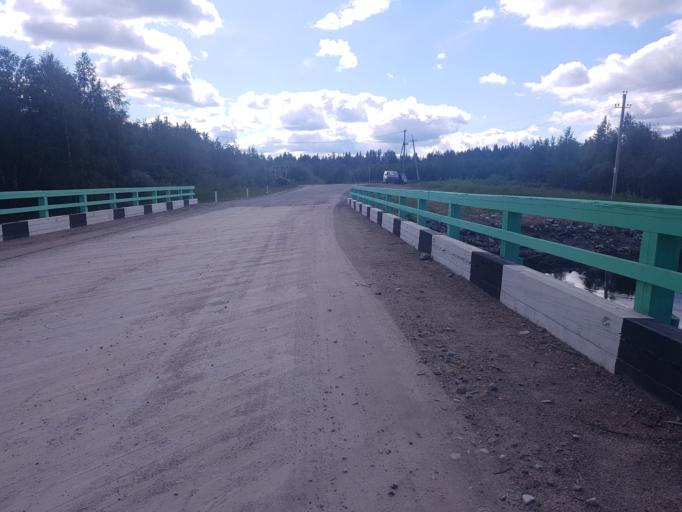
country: RU
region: Republic of Karelia
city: Kostomuksha
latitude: 64.8905
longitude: 30.5279
